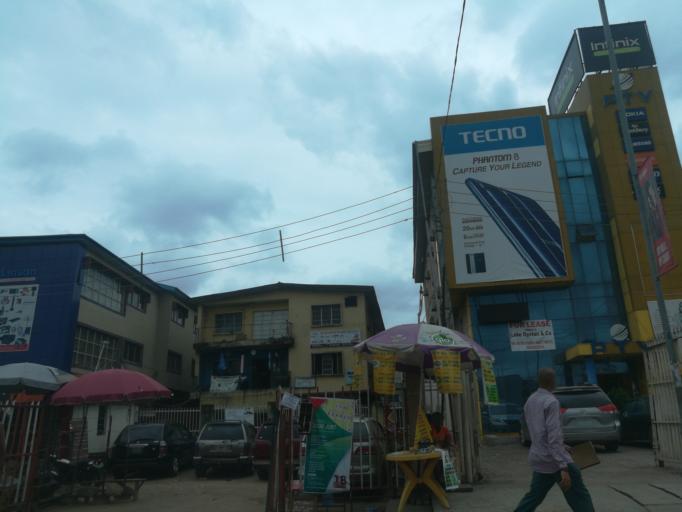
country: NG
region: Lagos
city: Ikeja
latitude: 6.5960
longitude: 3.3376
